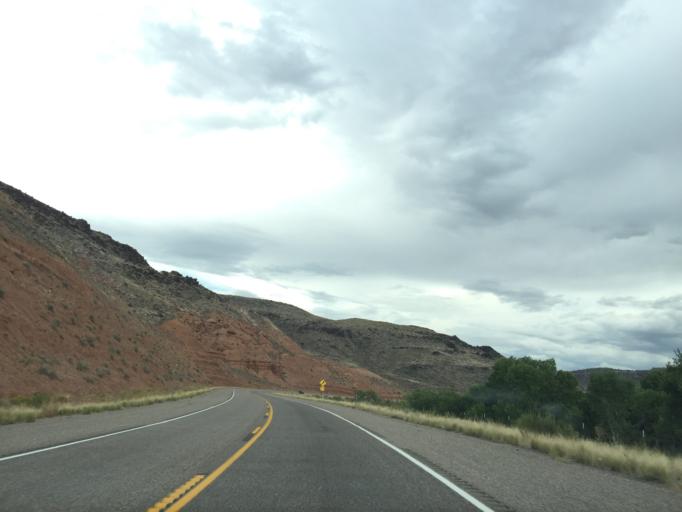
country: US
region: Utah
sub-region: Washington County
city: LaVerkin
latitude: 37.1790
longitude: -113.1212
